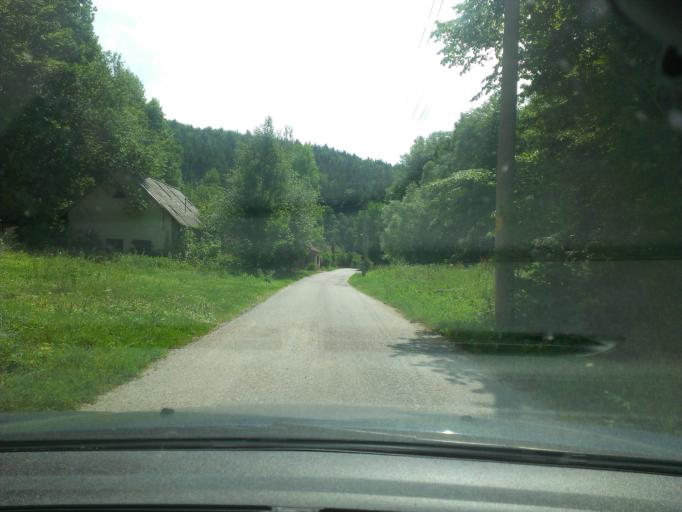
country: SK
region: Trenciansky
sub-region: Okres Myjava
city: Myjava
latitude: 48.8073
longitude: 17.5893
